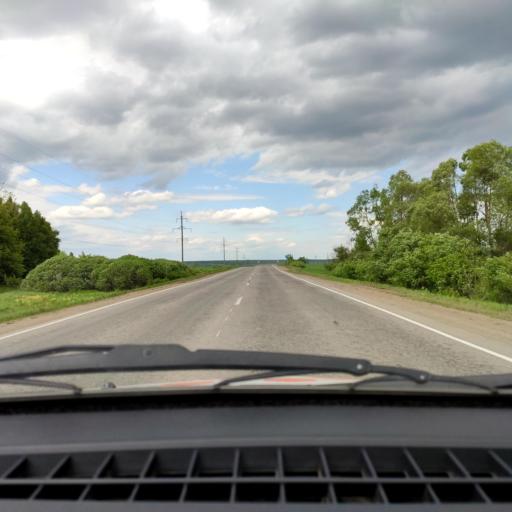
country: RU
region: Bashkortostan
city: Iglino
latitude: 54.8892
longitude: 56.4716
